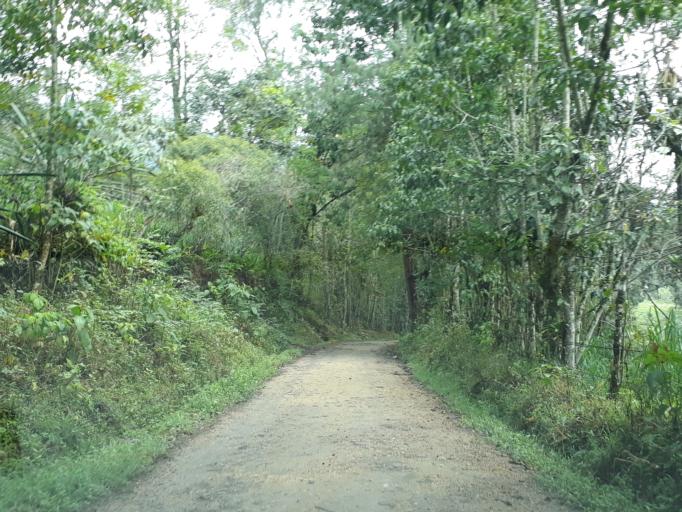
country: CO
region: Cundinamarca
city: Manta
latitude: 4.9799
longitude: -73.5606
